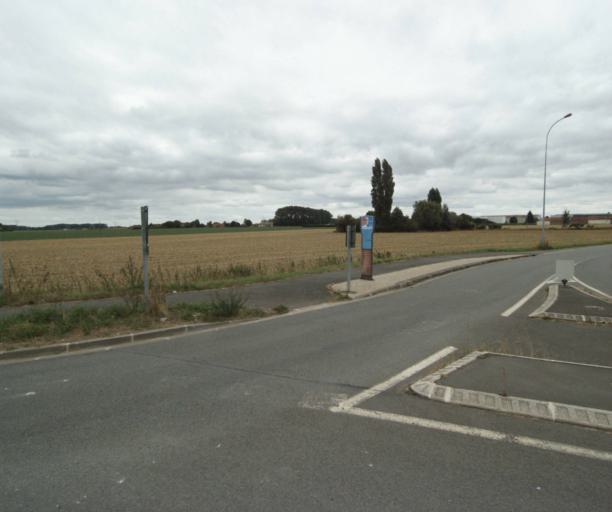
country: FR
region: Nord-Pas-de-Calais
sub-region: Departement du Nord
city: Avelin
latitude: 50.5476
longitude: 3.1003
